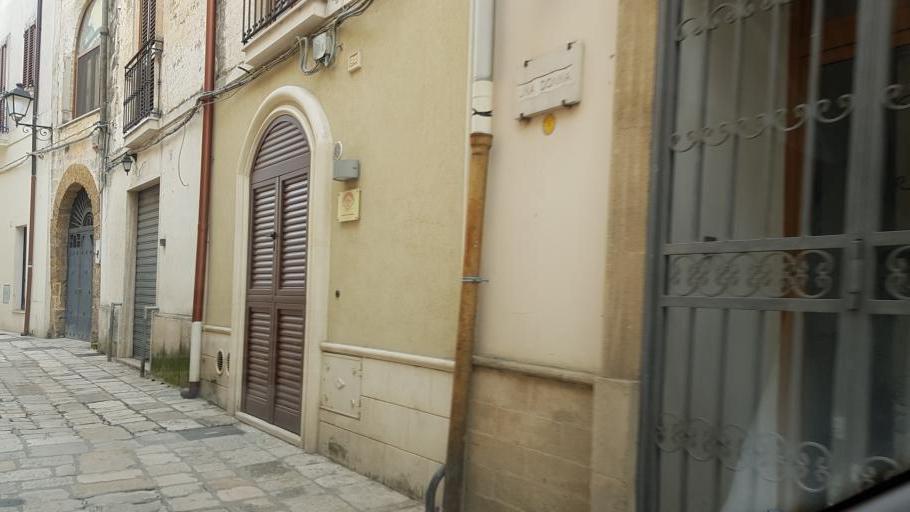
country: IT
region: Apulia
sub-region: Provincia di Brindisi
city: Mesagne
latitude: 40.5584
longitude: 17.8095
